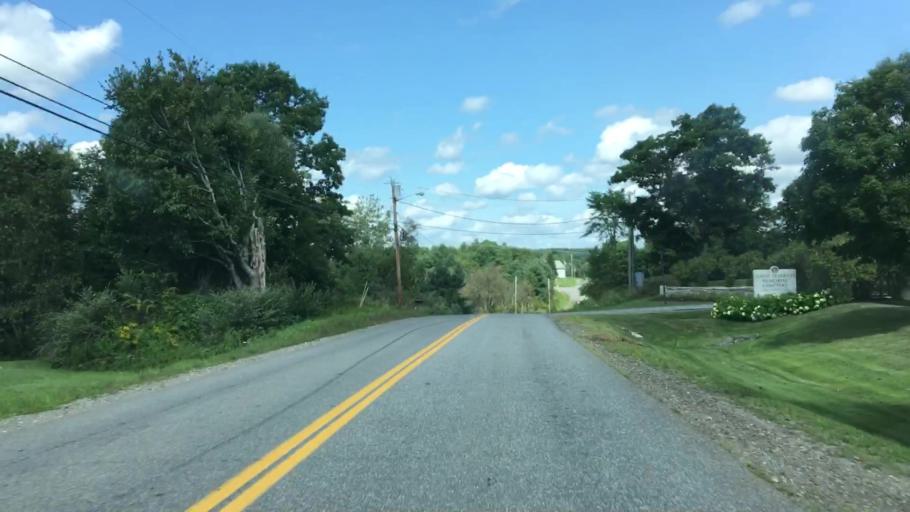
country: US
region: Maine
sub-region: Kennebec County
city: Manchester
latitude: 44.3521
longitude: -69.8145
